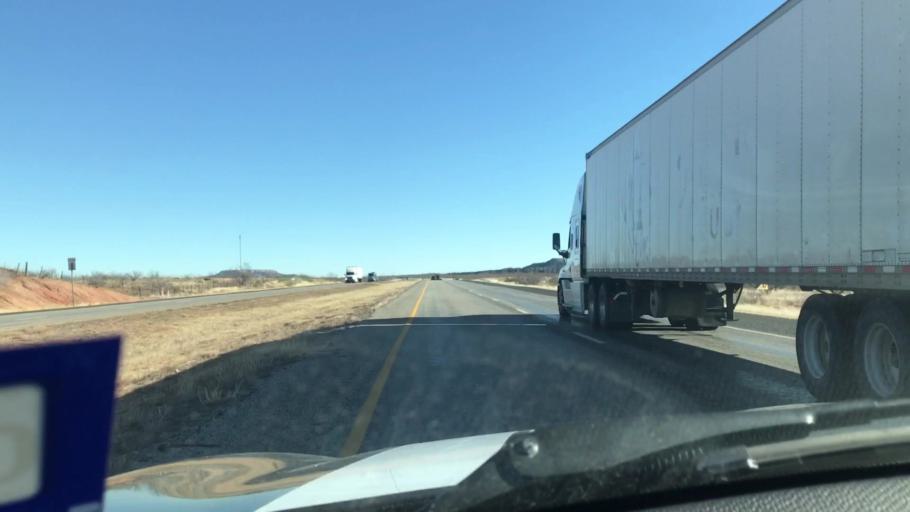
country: US
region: Texas
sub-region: Garza County
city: Post
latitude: 32.9928
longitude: -101.1457
